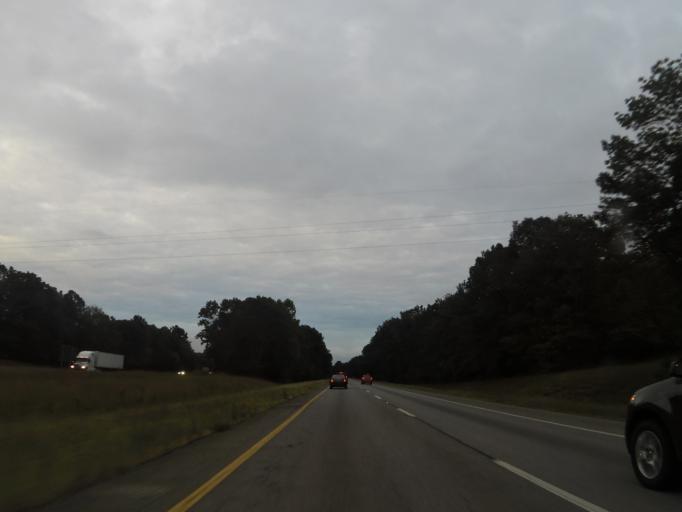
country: US
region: Alabama
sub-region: Saint Clair County
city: Ashville
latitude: 33.8655
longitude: -86.2808
